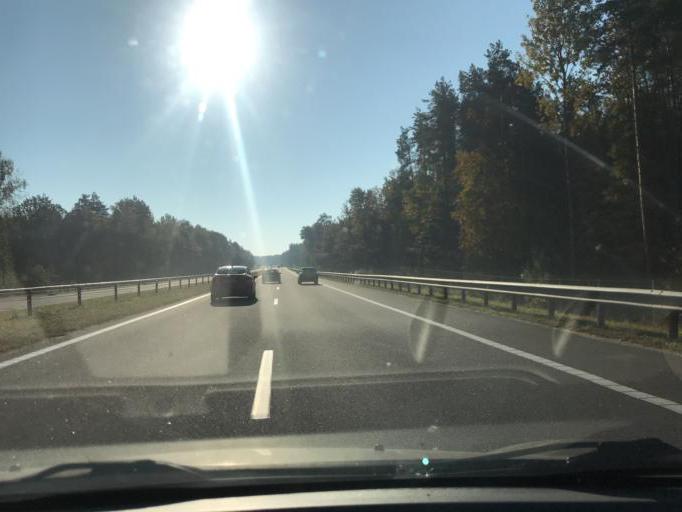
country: BY
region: Minsk
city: Pukhavichy
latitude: 53.5262
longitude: 28.2778
